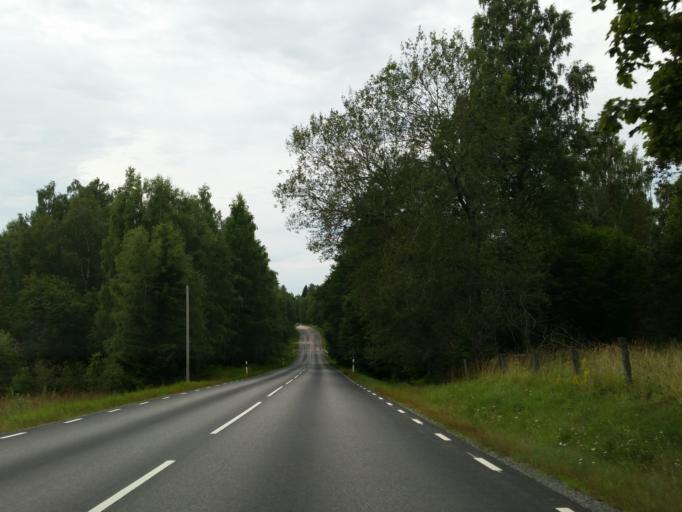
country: SE
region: Stockholm
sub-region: Sodertalje Kommun
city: Soedertaelje
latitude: 59.1945
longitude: 17.5299
